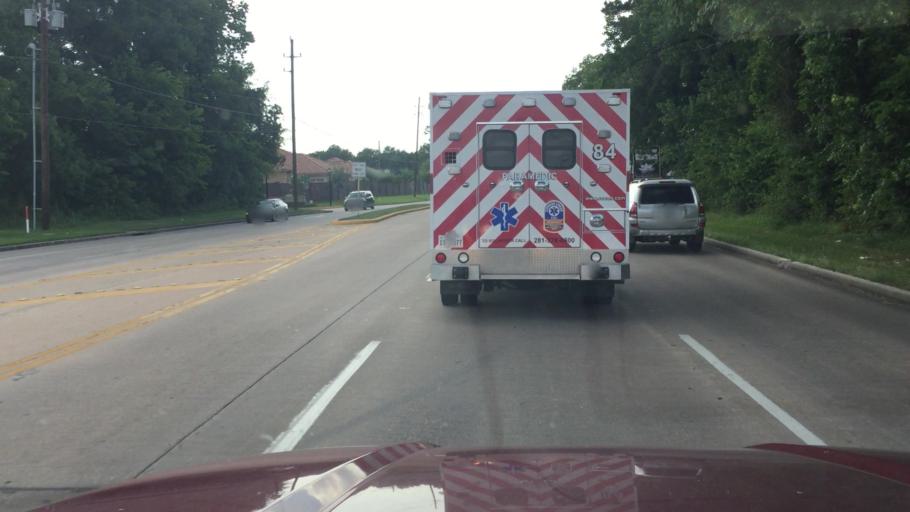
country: US
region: Texas
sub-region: Harris County
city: Tomball
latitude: 30.0239
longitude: -95.5274
